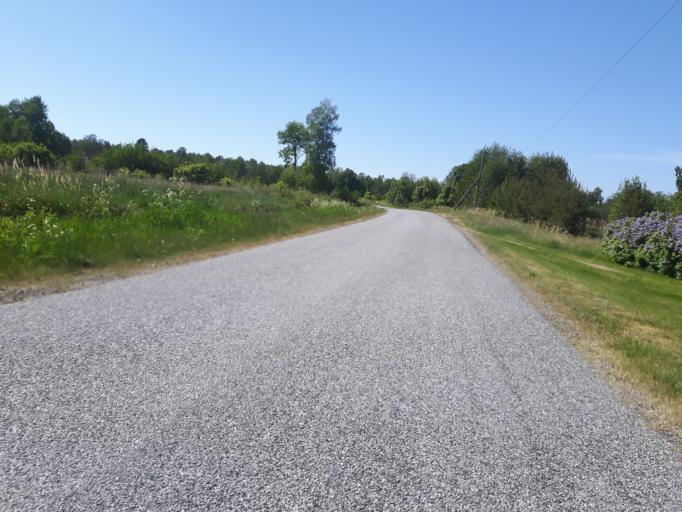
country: EE
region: Laeaene-Virumaa
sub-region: Haljala vald
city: Haljala
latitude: 59.5659
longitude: 26.3060
